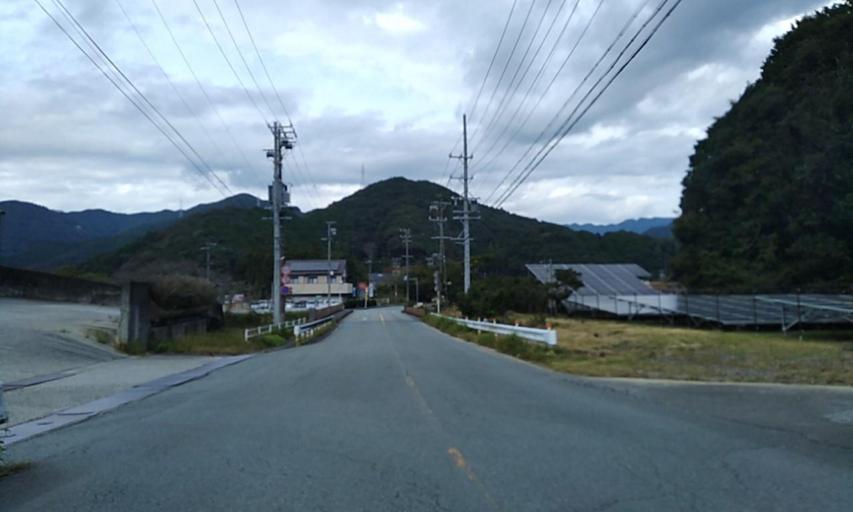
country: JP
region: Mie
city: Ise
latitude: 34.2756
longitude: 136.4922
